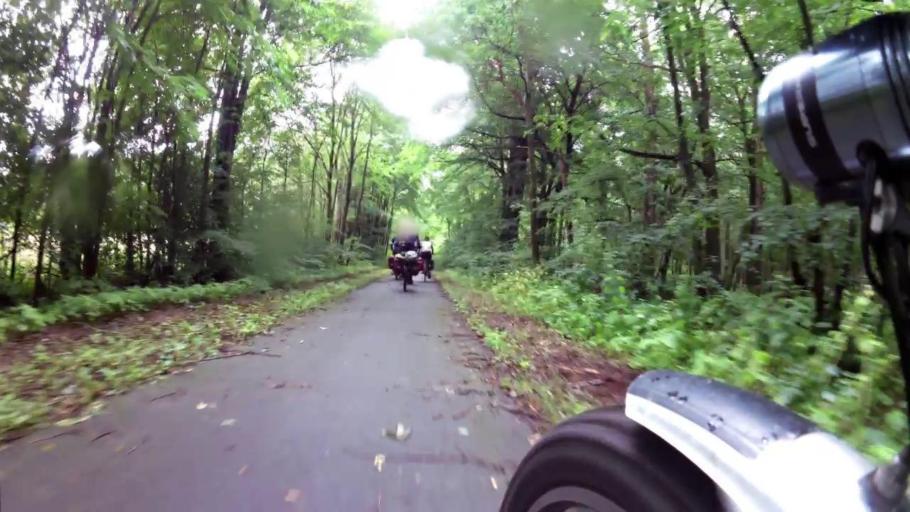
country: PL
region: West Pomeranian Voivodeship
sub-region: Powiat gryfinski
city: Banie
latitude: 53.0740
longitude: 14.6336
